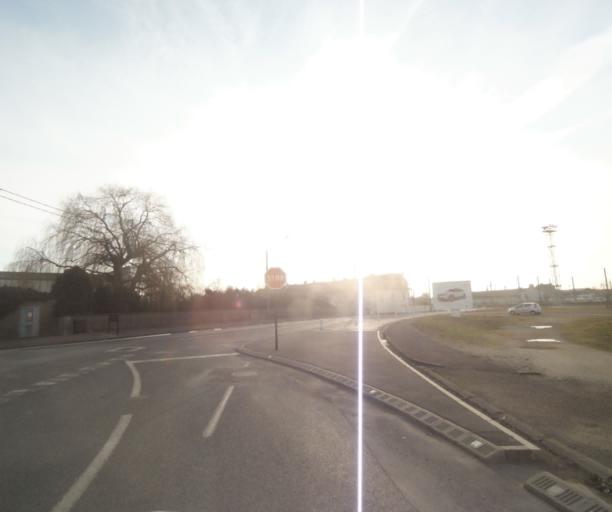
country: FR
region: Champagne-Ardenne
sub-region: Departement de la Haute-Marne
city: Saint-Dizier
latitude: 48.6450
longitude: 4.9452
